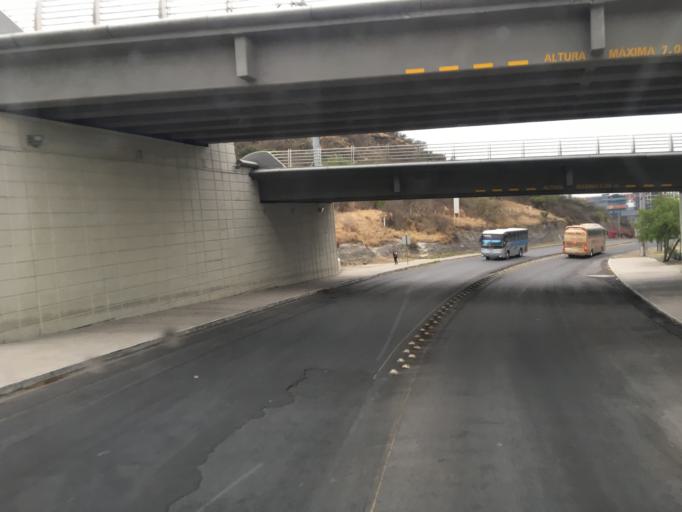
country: MX
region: Queretaro
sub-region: Queretaro
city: Santiago de Queretaro
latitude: 20.5822
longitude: -100.3563
